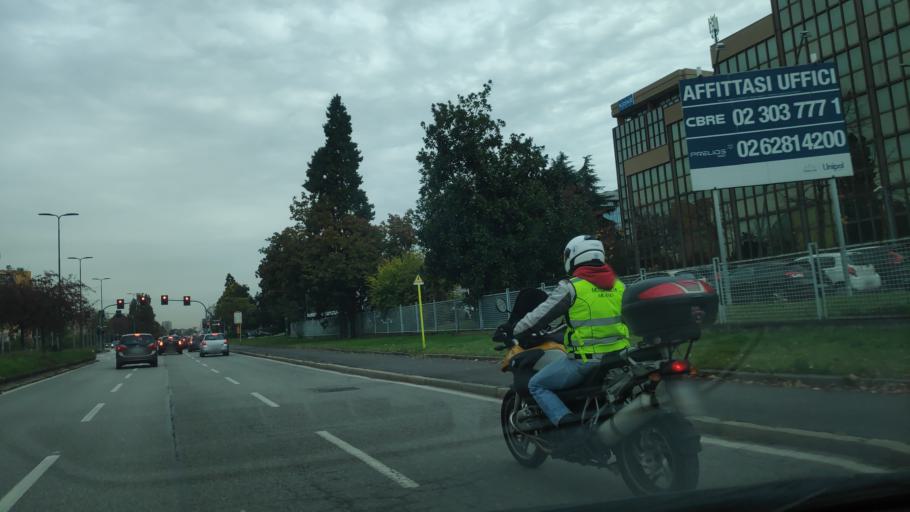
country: IT
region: Lombardy
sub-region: Citta metropolitana di Milano
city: Rozzano
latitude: 45.4093
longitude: 9.1747
